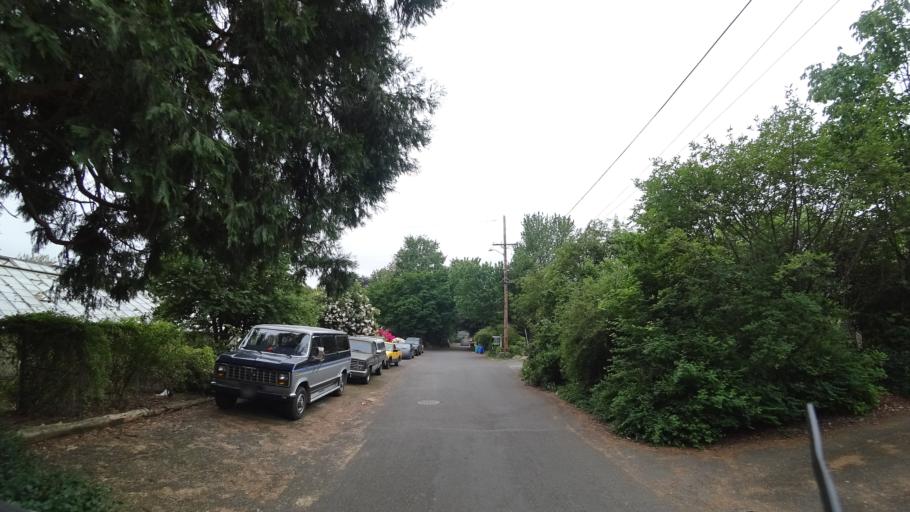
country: US
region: Oregon
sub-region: Multnomah County
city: Lents
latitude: 45.5003
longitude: -122.6190
